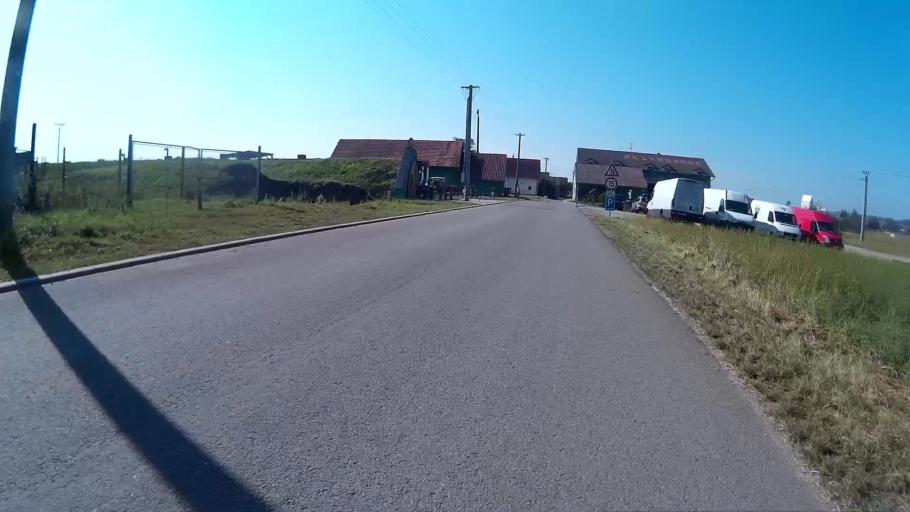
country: CZ
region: South Moravian
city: Novosedly
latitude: 48.8352
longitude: 16.5045
